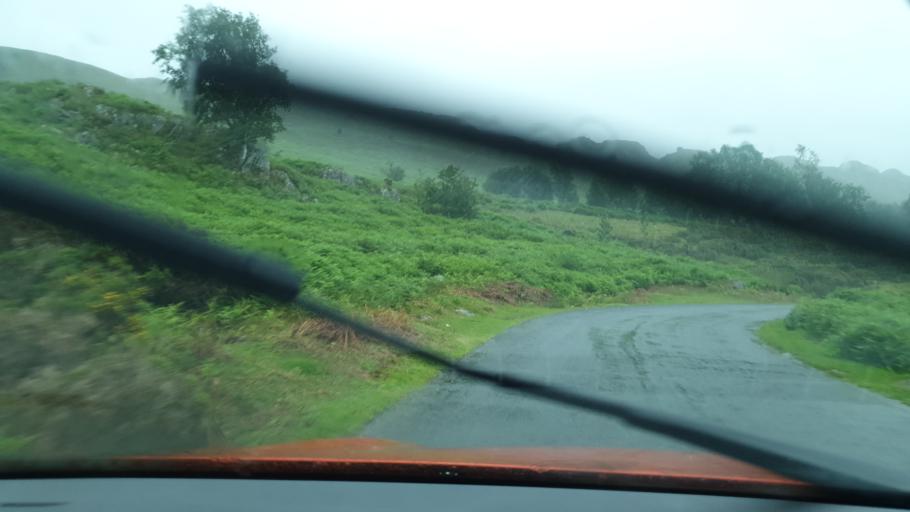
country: GB
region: England
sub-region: Cumbria
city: Millom
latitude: 54.3139
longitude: -3.2300
